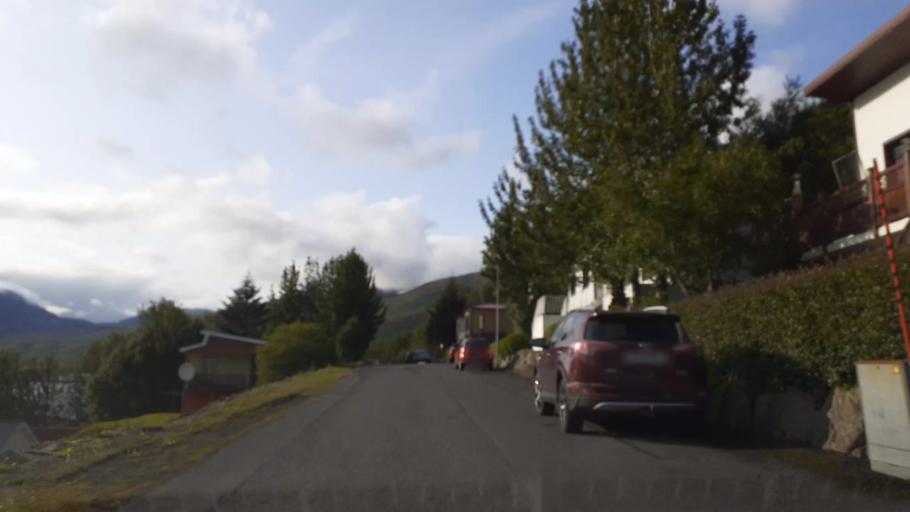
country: IS
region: East
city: Eskifjoerdur
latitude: 65.0666
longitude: -14.0027
